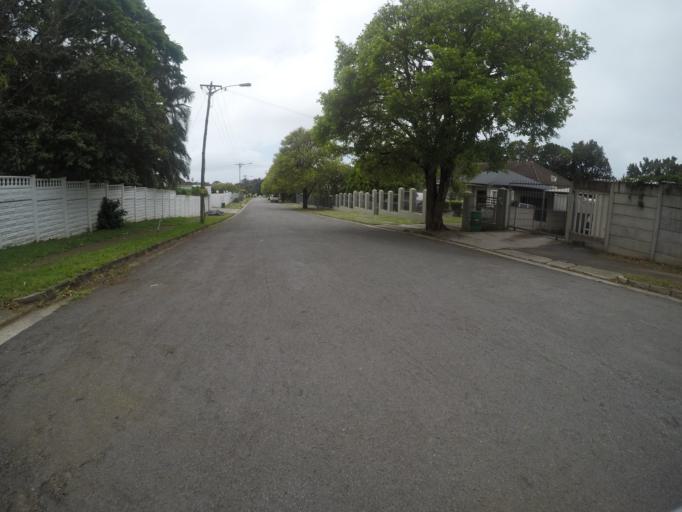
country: ZA
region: Eastern Cape
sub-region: Buffalo City Metropolitan Municipality
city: East London
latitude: -32.9887
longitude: 27.9204
